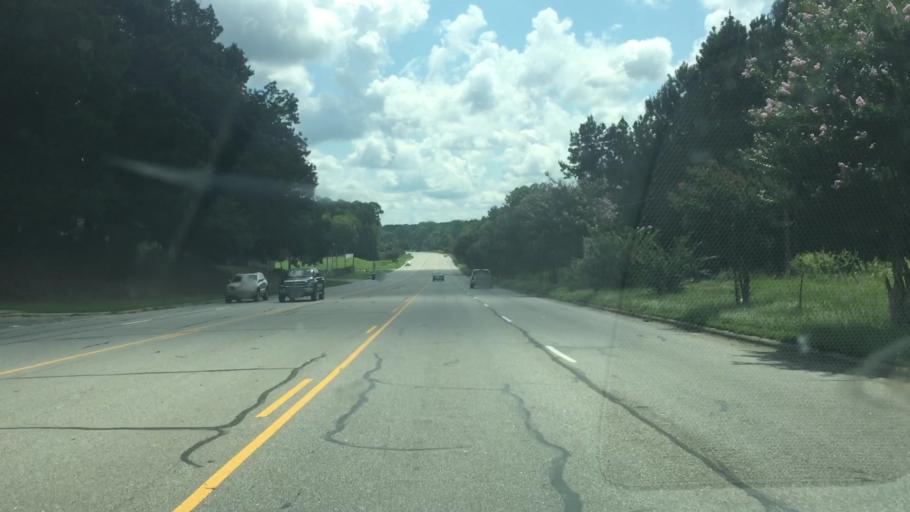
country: US
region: North Carolina
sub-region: Anson County
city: Wadesboro
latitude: 34.9637
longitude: -80.0457
